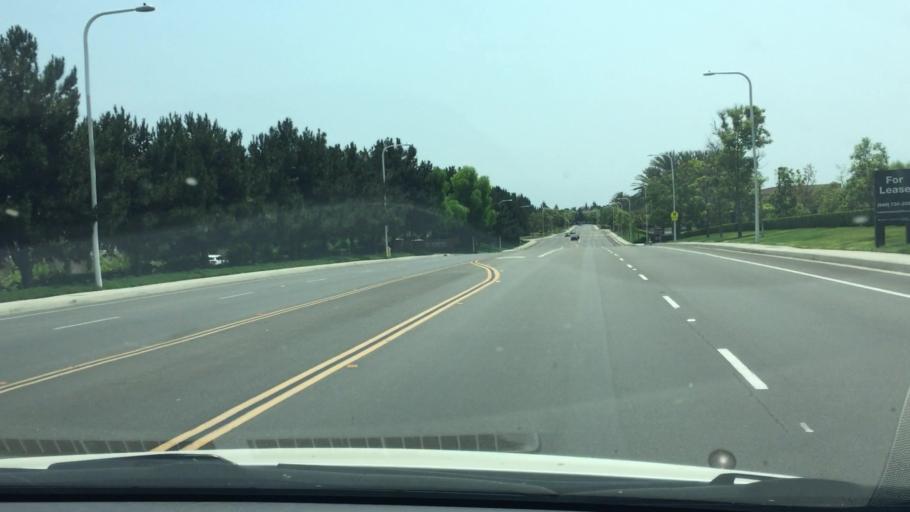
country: US
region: California
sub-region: Orange County
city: North Tustin
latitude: 33.7187
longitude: -117.7872
